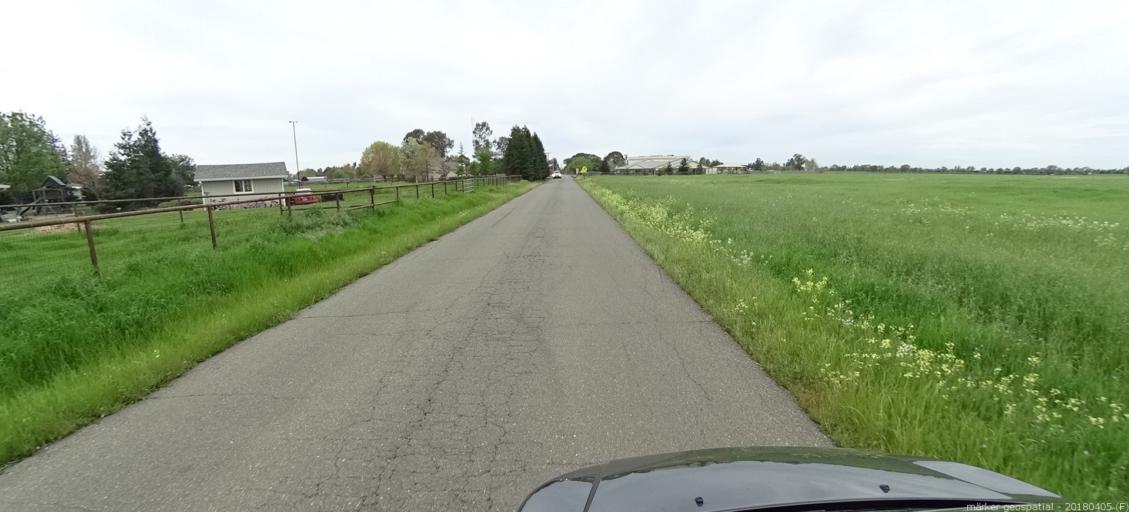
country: US
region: California
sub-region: Sacramento County
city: Herald
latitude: 38.2926
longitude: -121.2373
